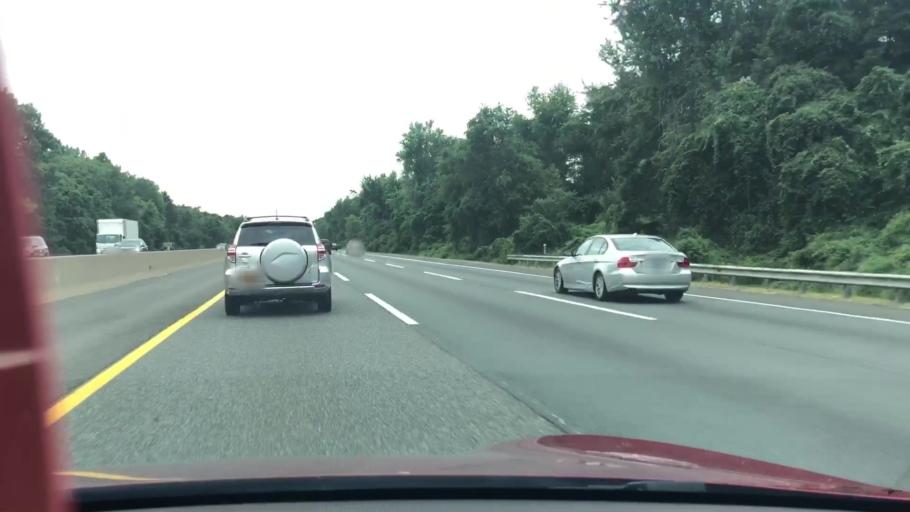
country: US
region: New Jersey
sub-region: Burlington County
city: Mount Holly
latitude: 40.0540
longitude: -74.7863
